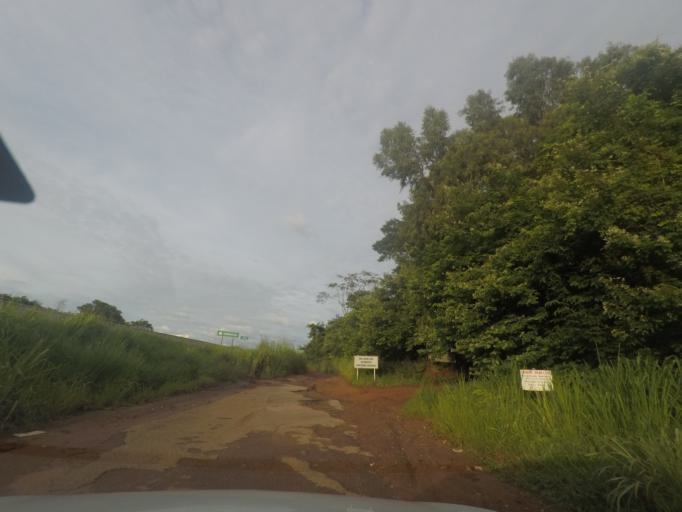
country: BR
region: Goias
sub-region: Trindade
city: Trindade
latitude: -16.7368
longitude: -49.4057
